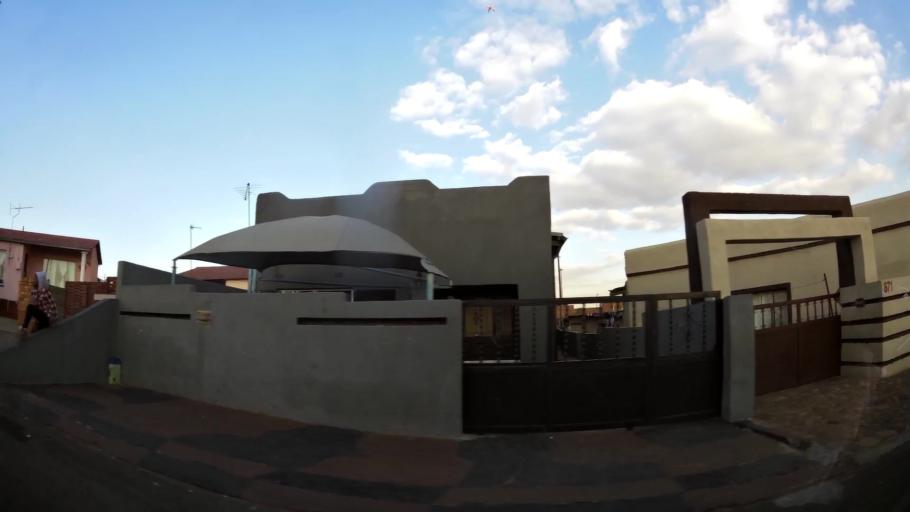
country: ZA
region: Gauteng
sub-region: West Rand District Municipality
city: Krugersdorp
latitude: -26.0803
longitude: 27.7561
